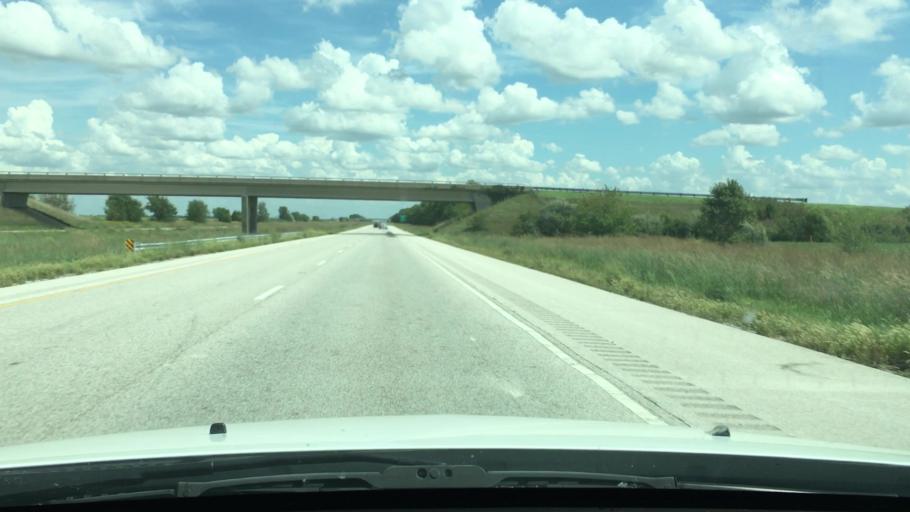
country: US
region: Illinois
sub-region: Scott County
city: Winchester
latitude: 39.6802
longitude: -90.3484
